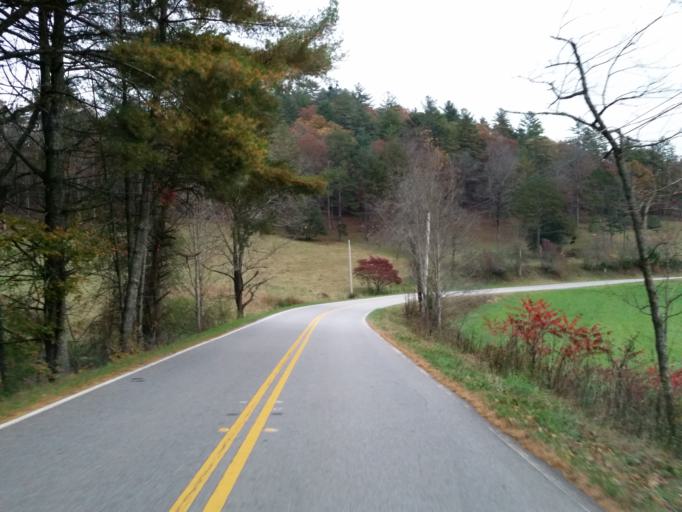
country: US
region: Georgia
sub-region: Union County
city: Blairsville
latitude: 34.7275
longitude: -84.0820
